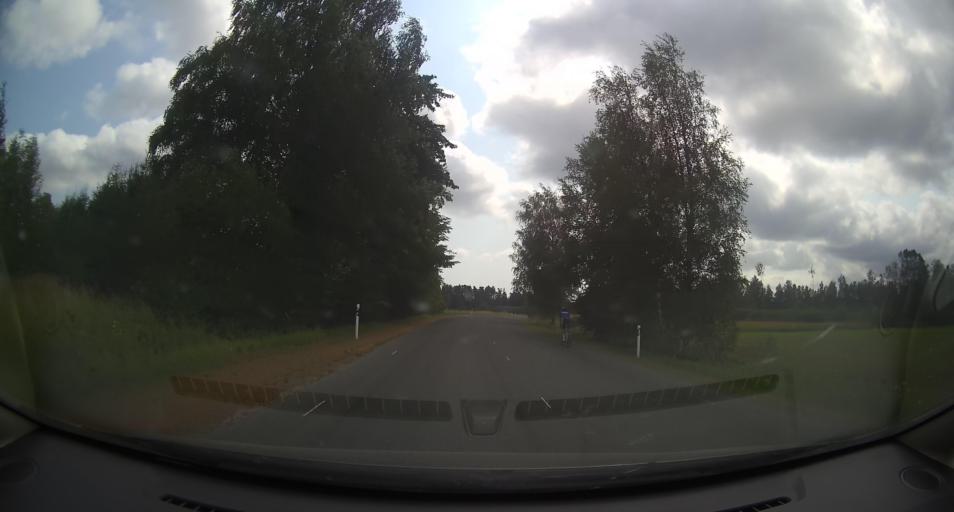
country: EE
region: Paernumaa
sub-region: Audru vald
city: Audru
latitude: 58.4366
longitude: 24.3099
